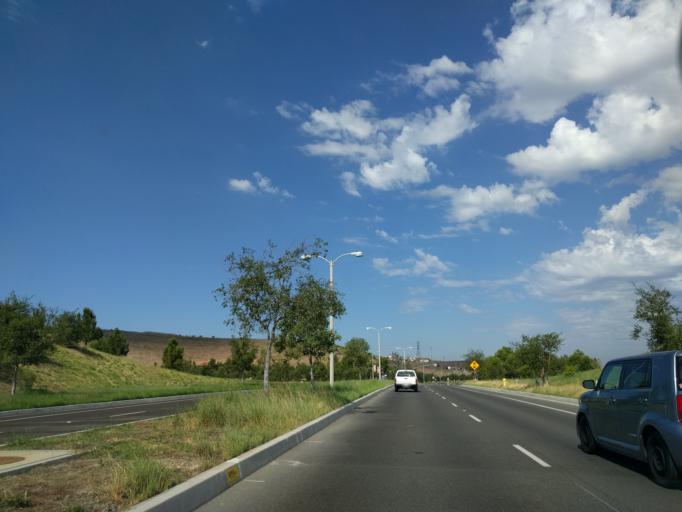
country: US
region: California
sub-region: Orange County
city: Laguna Woods
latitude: 33.6362
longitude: -117.7537
